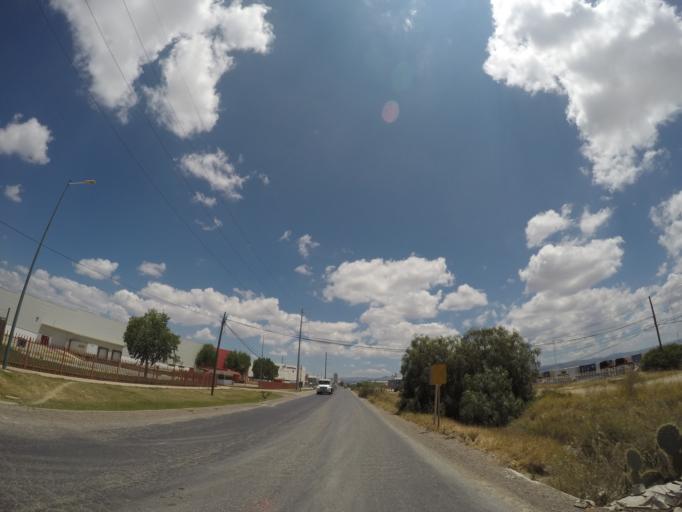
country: MX
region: San Luis Potosi
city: La Pila
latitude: 22.0413
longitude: -100.8864
